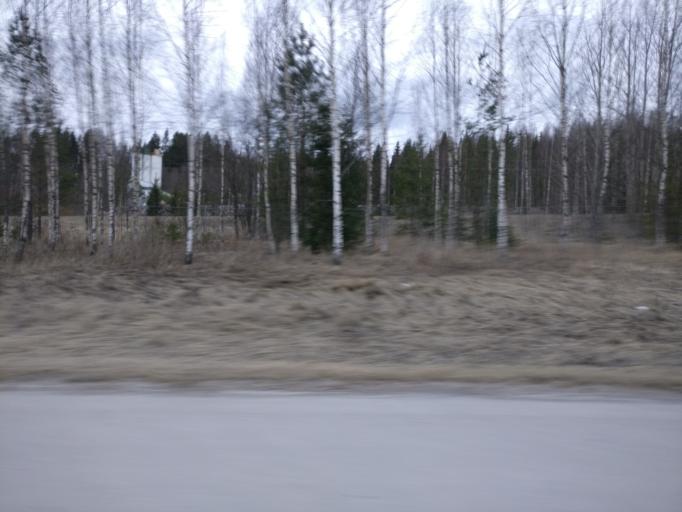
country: FI
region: Uusimaa
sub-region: Helsinki
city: Nurmijaervi
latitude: 60.4095
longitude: 24.8232
